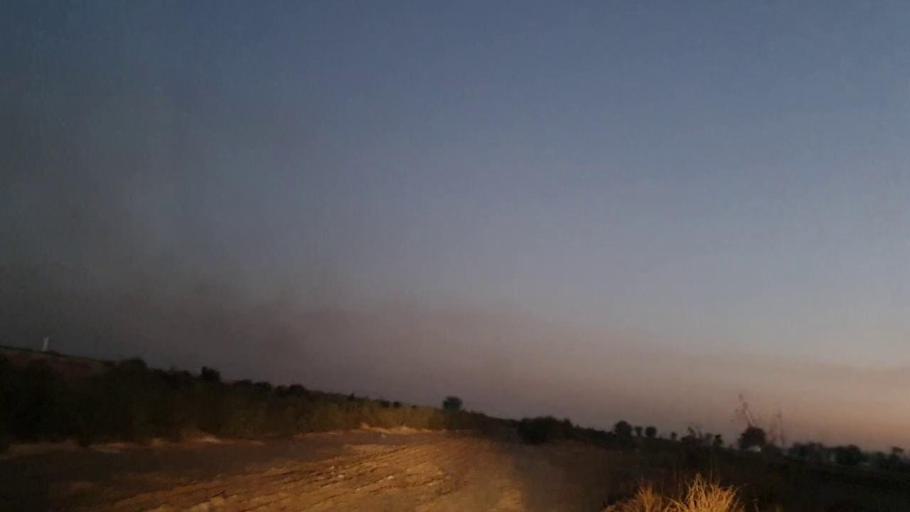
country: PK
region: Sindh
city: Nawabshah
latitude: 26.3309
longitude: 68.3750
